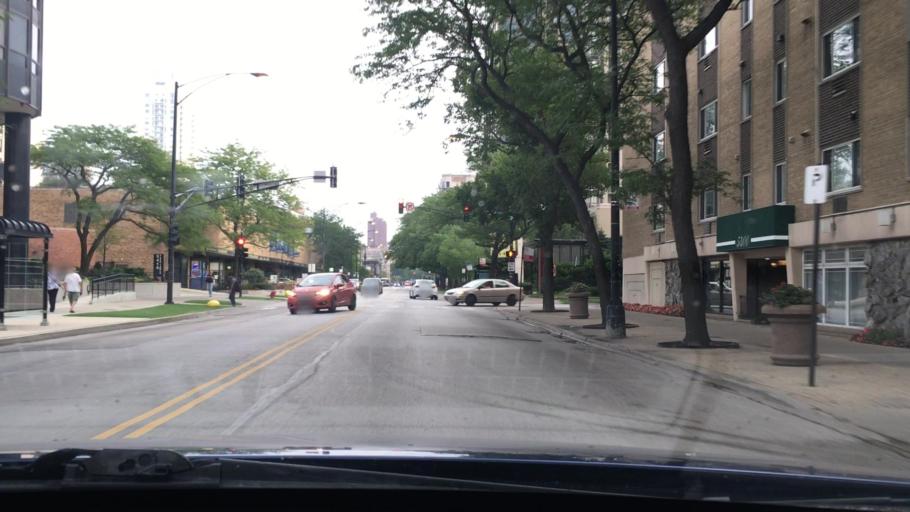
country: US
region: Illinois
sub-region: Cook County
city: Evanston
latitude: 41.9805
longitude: -87.6551
